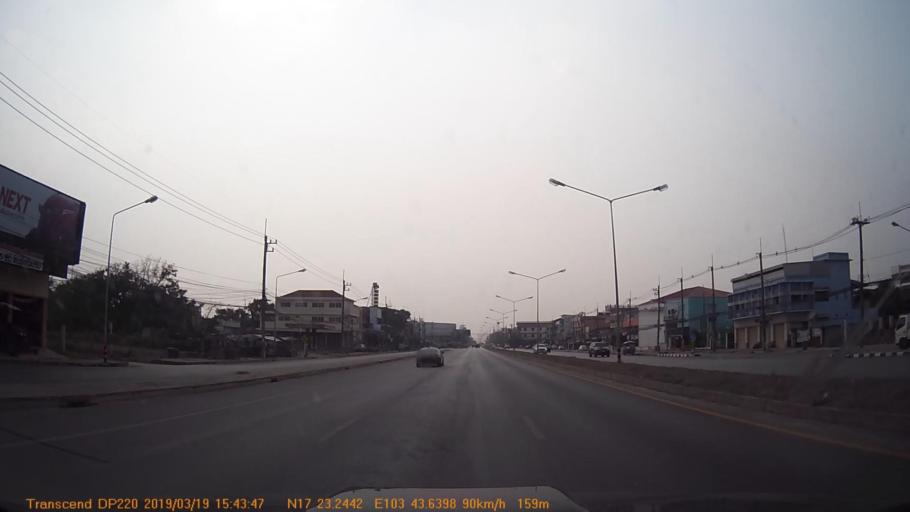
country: TH
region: Sakon Nakhon
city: Phang Khon
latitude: 17.3874
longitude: 103.7273
